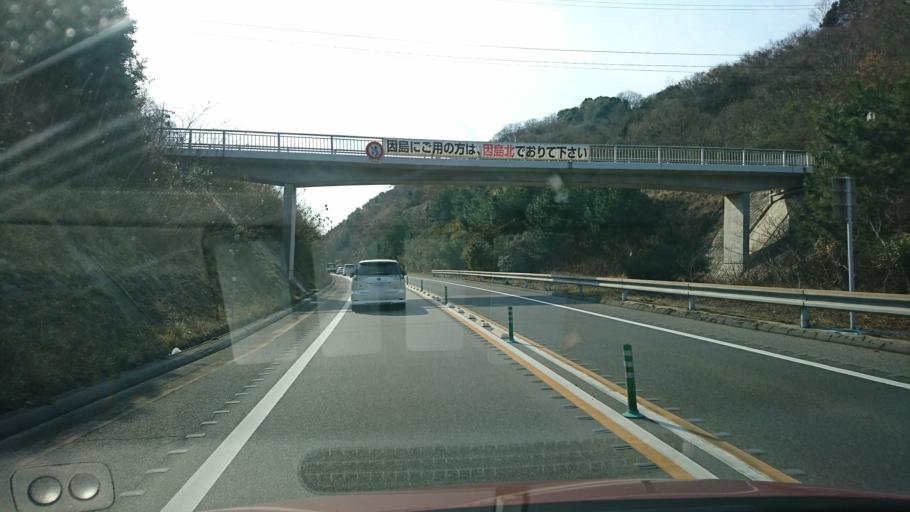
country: JP
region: Hiroshima
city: Innoshima
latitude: 34.3454
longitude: 133.1620
